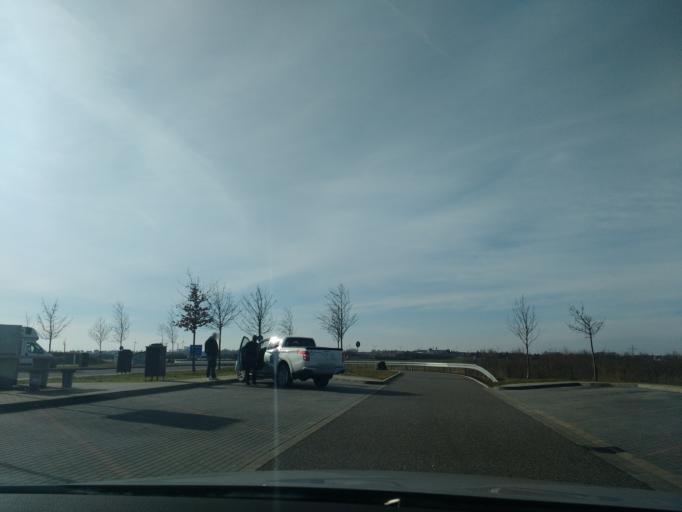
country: DE
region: Saxony-Anhalt
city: Granschutz
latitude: 51.2099
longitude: 12.0298
